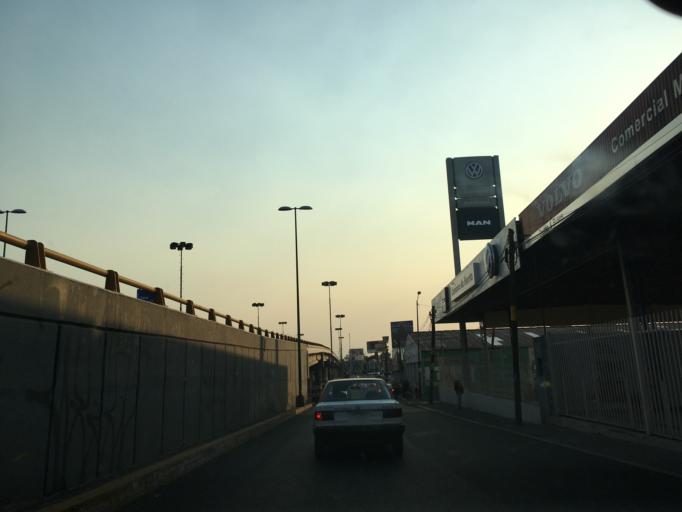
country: MX
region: Michoacan
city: Morelia
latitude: 19.7111
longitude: -101.1641
